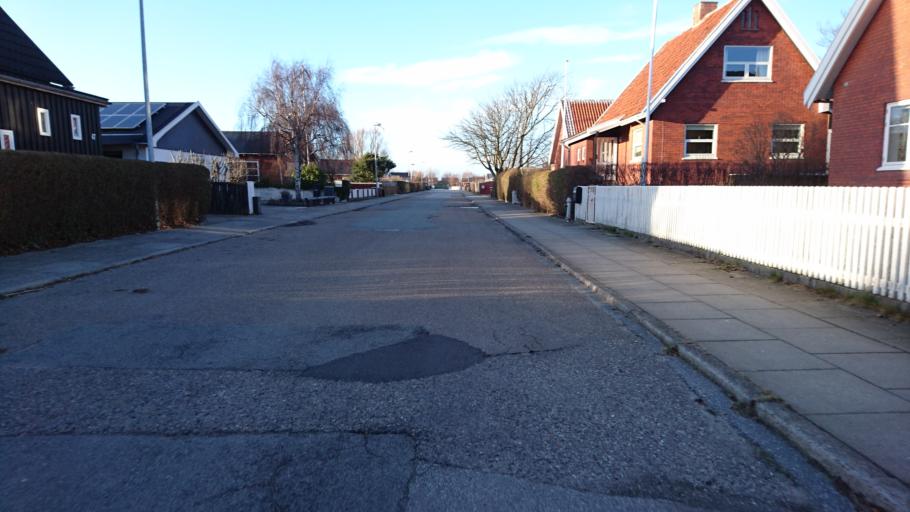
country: DK
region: North Denmark
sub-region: Frederikshavn Kommune
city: Skagen
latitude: 57.7290
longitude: 10.5886
